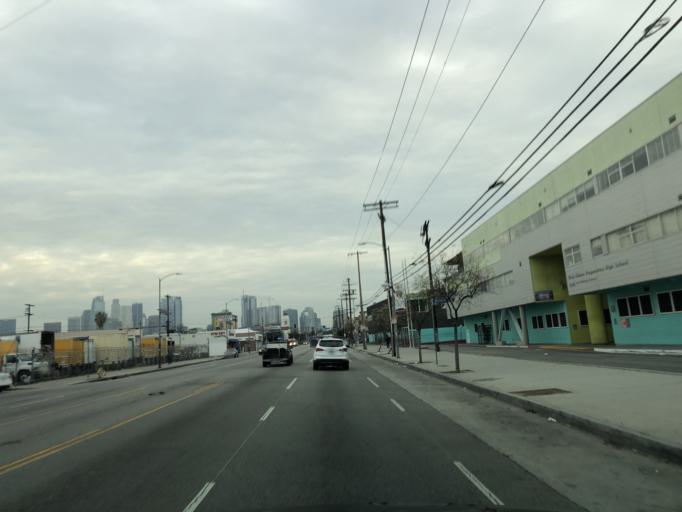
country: US
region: California
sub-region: Los Angeles County
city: Los Angeles
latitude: 34.0400
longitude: -118.2901
